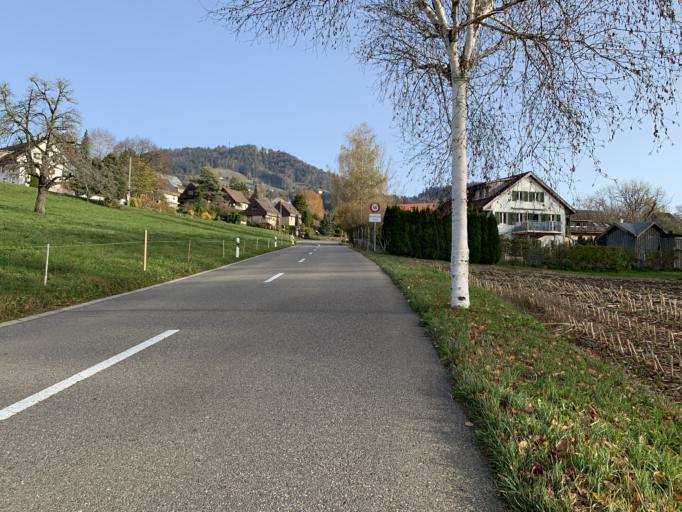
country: CH
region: Zurich
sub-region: Bezirk Hinwil
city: Hadlikon
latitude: 47.2975
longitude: 8.8595
